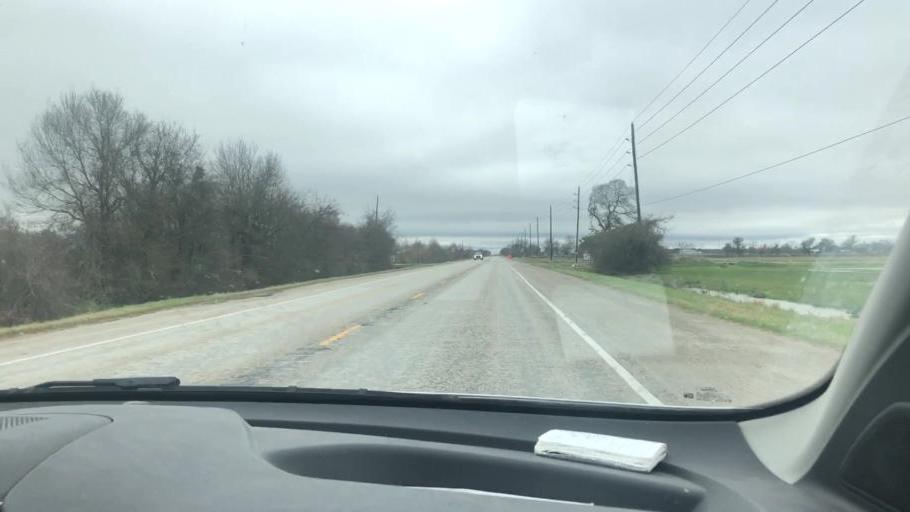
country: US
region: Texas
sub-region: Wharton County
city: Wharton
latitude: 29.2731
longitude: -96.0617
